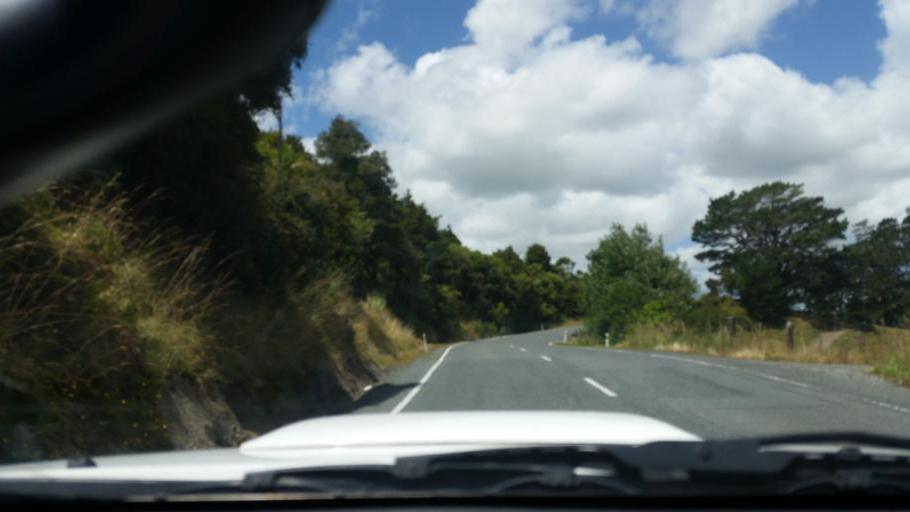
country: NZ
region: Northland
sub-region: Whangarei
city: Ruakaka
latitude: -36.0768
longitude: 174.2553
